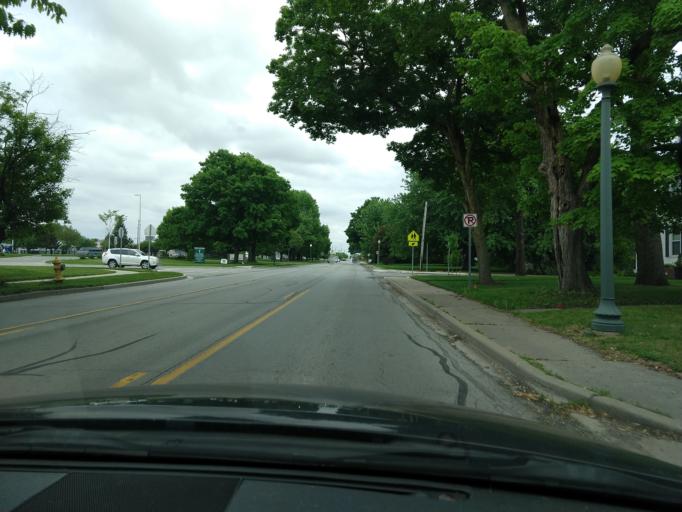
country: US
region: Indiana
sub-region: Hamilton County
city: Noblesville
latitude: 40.0455
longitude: -86.0040
